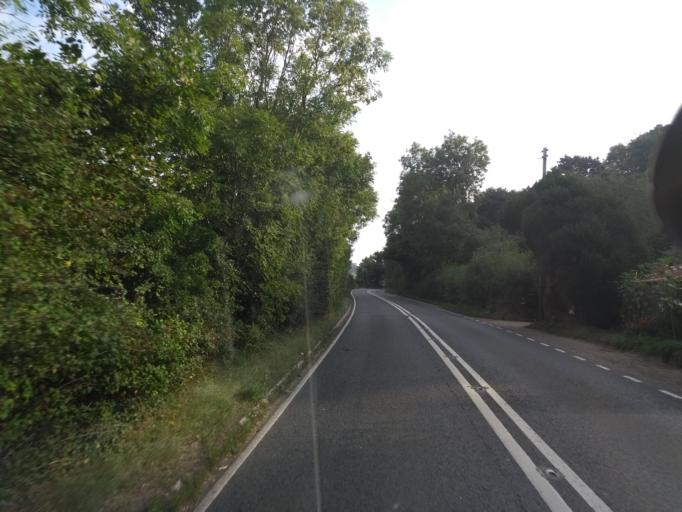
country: GB
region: England
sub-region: Devon
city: Colyton
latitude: 50.7850
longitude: -3.0627
